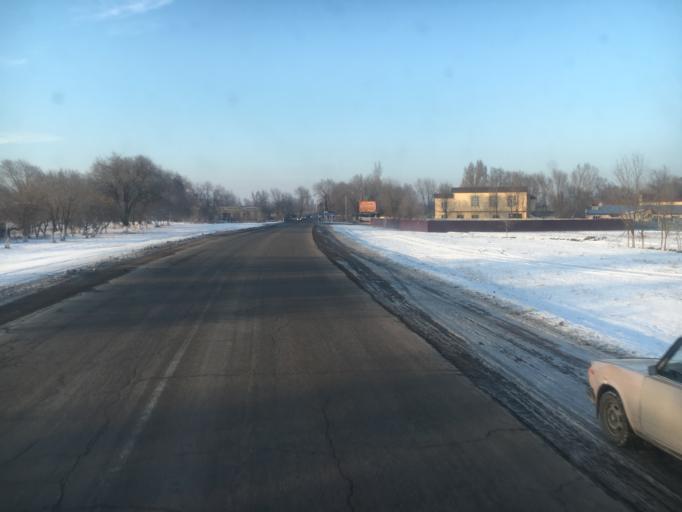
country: KZ
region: Almaty Oblysy
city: Burunday
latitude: 43.3646
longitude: 76.6420
